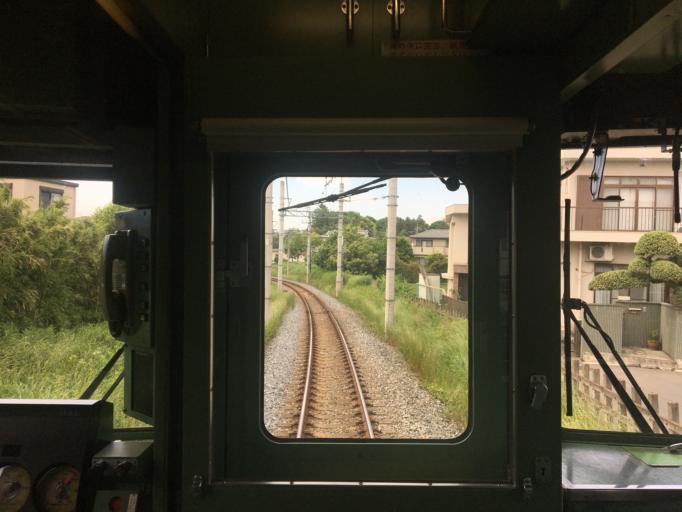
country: JP
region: Saitama
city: Yorii
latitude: 36.1099
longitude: 139.2333
